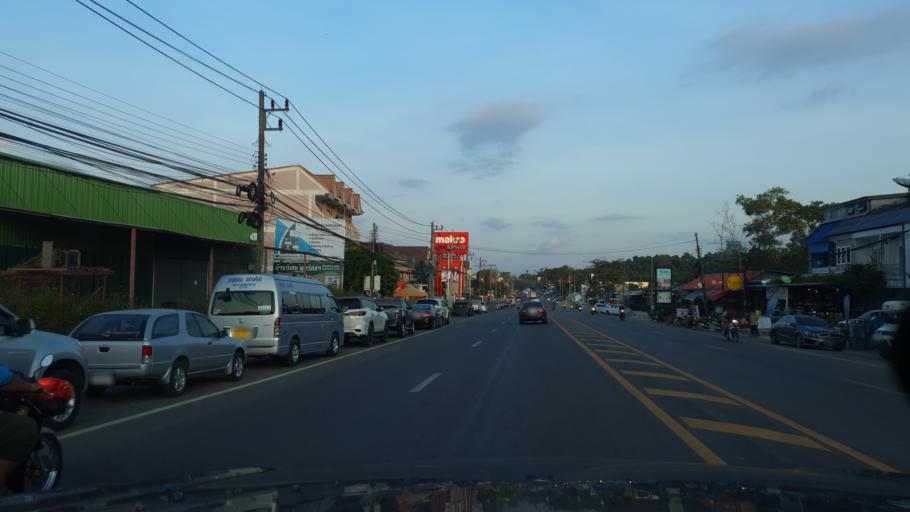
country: TH
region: Phangnga
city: Ban Ao Nang
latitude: 8.0417
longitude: 98.8394
